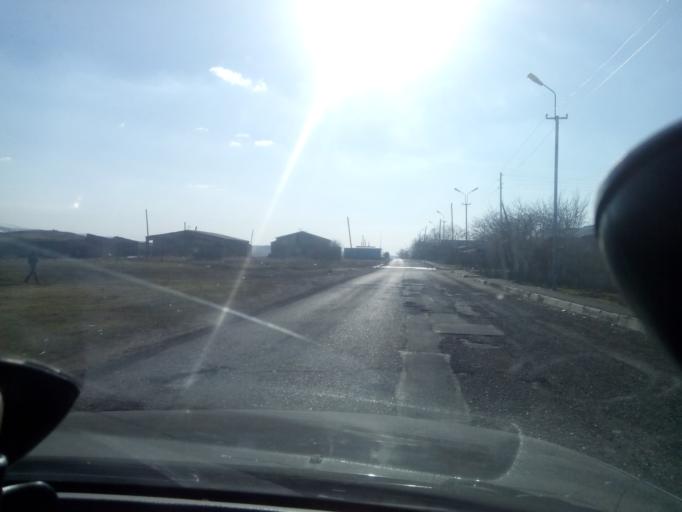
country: AM
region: Kotayk'i Marz
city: Zarr
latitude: 40.2569
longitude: 44.7390
